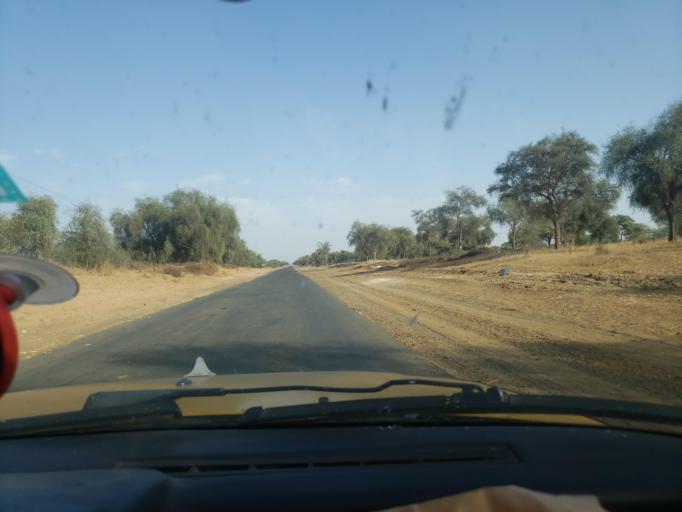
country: SN
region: Louga
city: Louga
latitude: 15.5075
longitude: -15.9697
